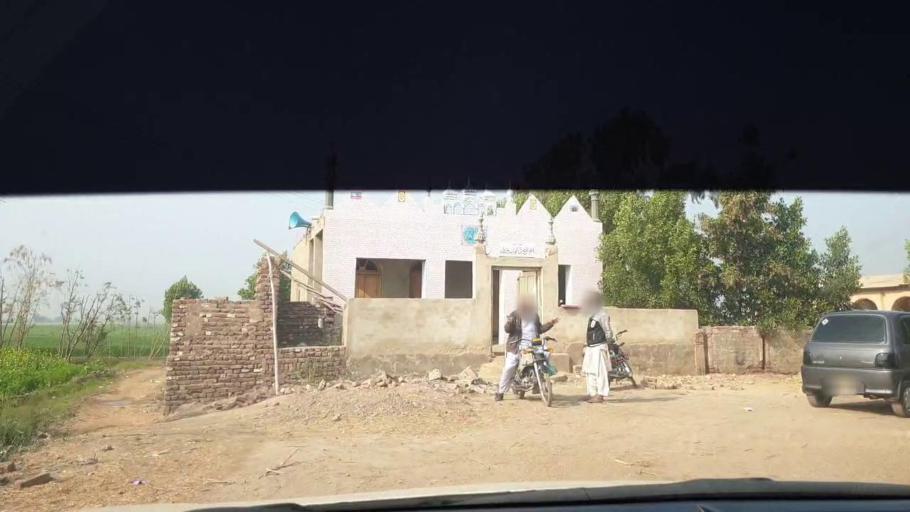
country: PK
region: Sindh
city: Berani
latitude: 25.7763
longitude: 68.7986
